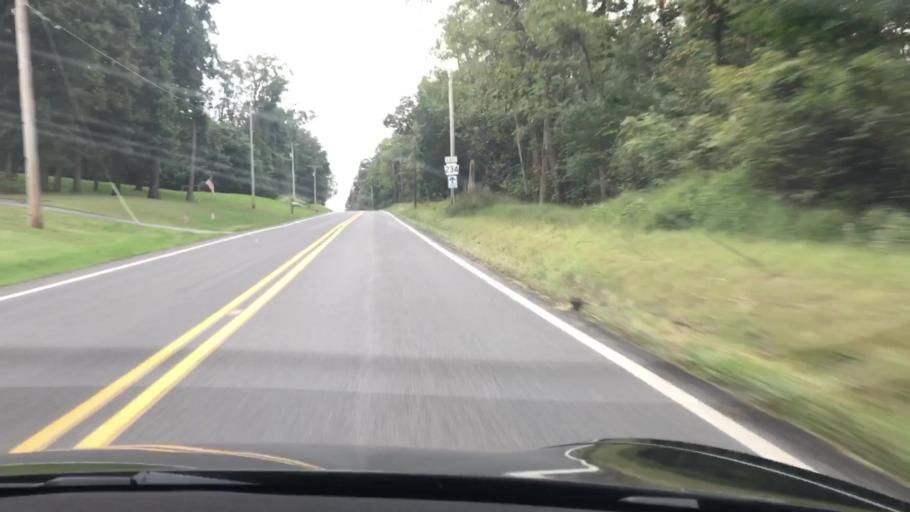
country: US
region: Pennsylvania
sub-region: Adams County
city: Lake Meade
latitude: 39.9494
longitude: -77.1310
